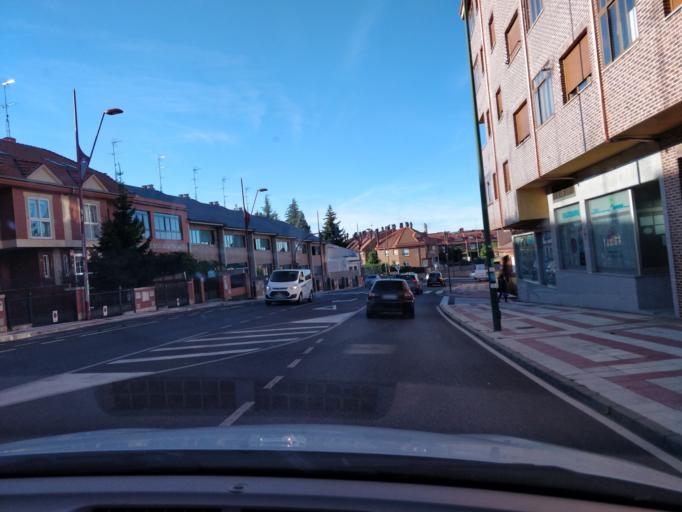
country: ES
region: Castille and Leon
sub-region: Provincia de Leon
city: San Andres del Rabanedo
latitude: 42.5944
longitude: -5.6120
